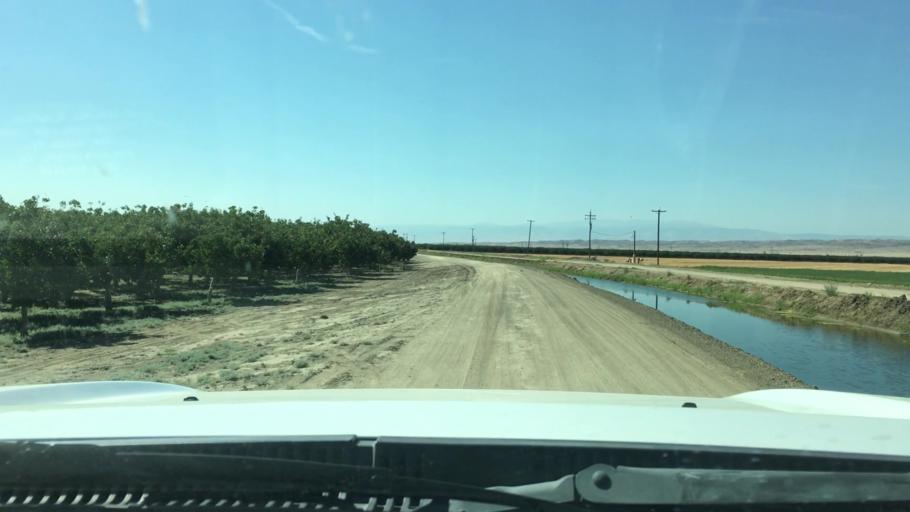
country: US
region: California
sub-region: Kern County
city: Buttonwillow
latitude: 35.3691
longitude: -119.3985
